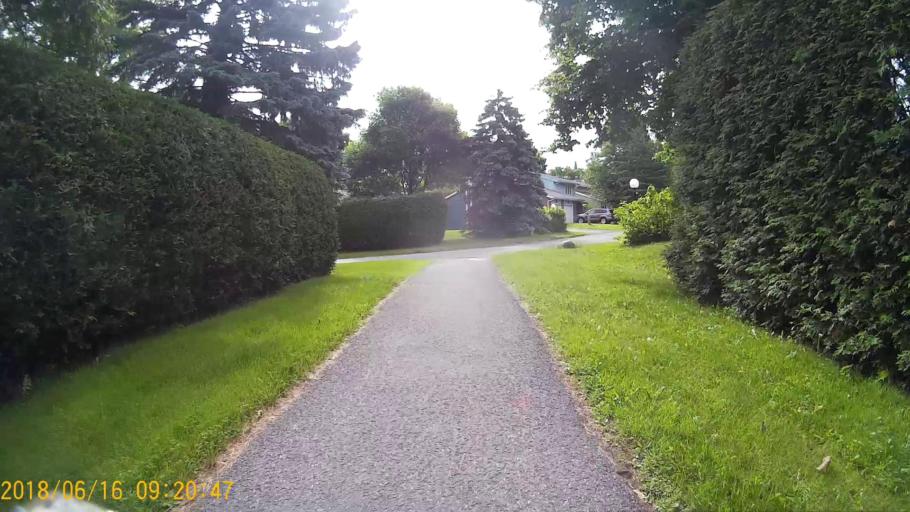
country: CA
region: Ontario
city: Bells Corners
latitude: 45.3124
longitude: -75.8930
